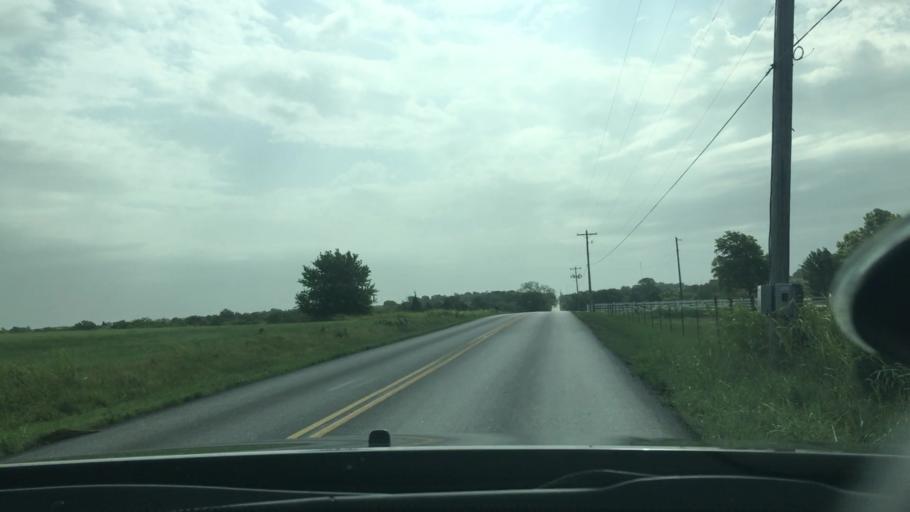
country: US
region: Oklahoma
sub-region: Carter County
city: Ardmore
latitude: 34.2020
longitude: -97.1945
